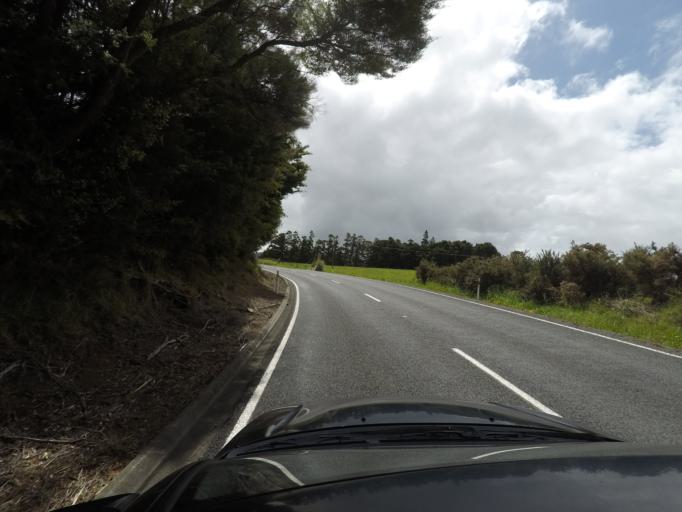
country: NZ
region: Auckland
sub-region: Auckland
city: Parakai
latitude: -36.5031
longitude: 174.5051
